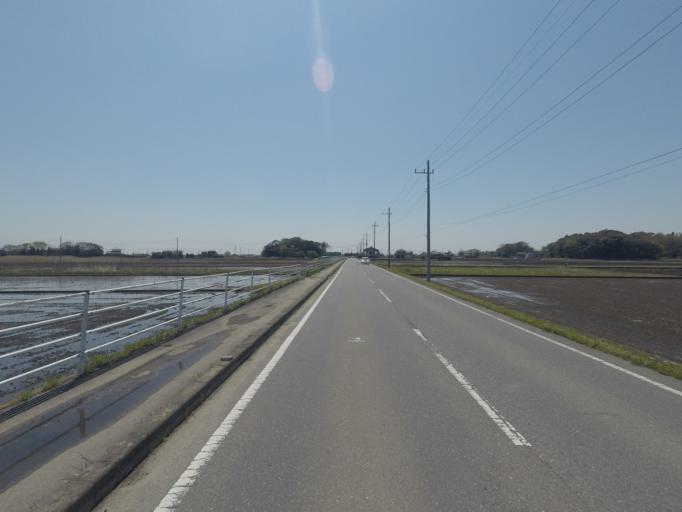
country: JP
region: Ibaraki
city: Ushiku
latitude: 35.9504
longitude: 140.1020
